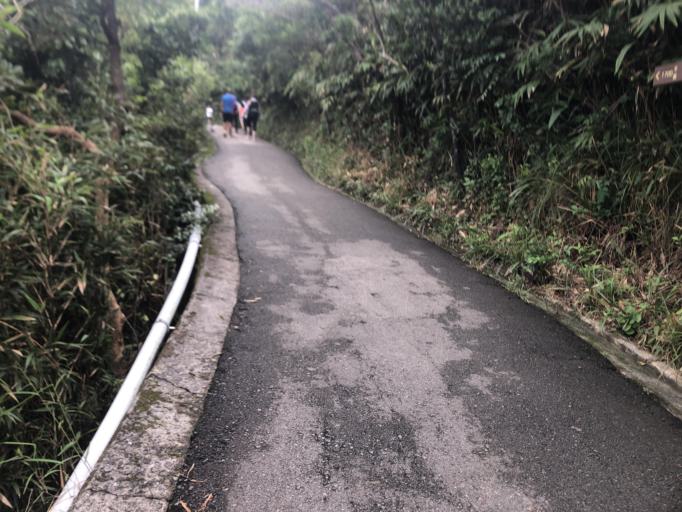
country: HK
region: Central and Western
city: Central
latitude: 22.2763
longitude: 114.1374
